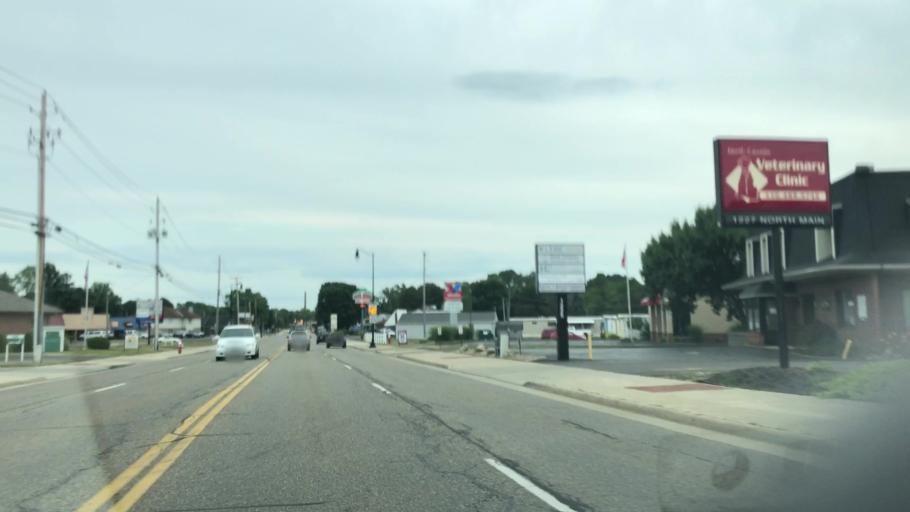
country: US
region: Ohio
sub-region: Stark County
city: North Canton
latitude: 40.8890
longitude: -81.4055
